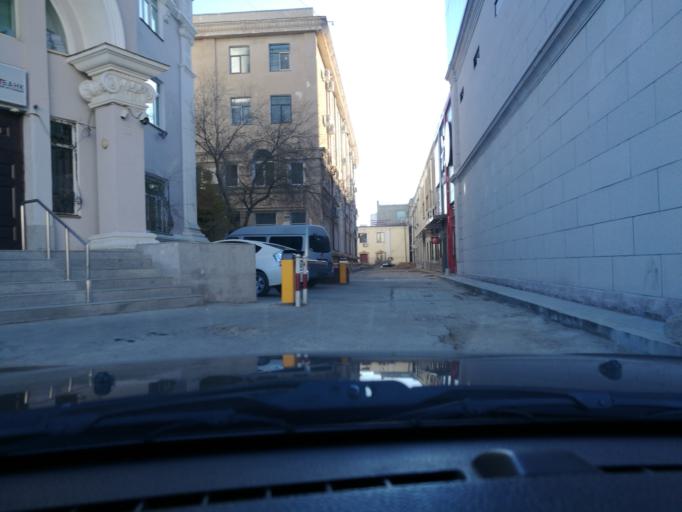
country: MN
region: Ulaanbaatar
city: Ulaanbaatar
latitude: 47.9212
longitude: 106.9189
